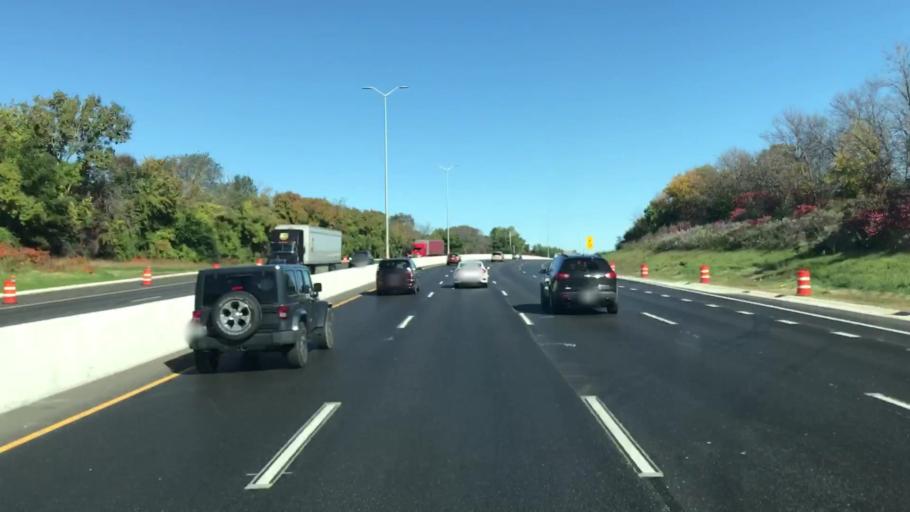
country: US
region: Wisconsin
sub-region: Milwaukee County
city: Greenfield
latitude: 42.9751
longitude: -88.0388
